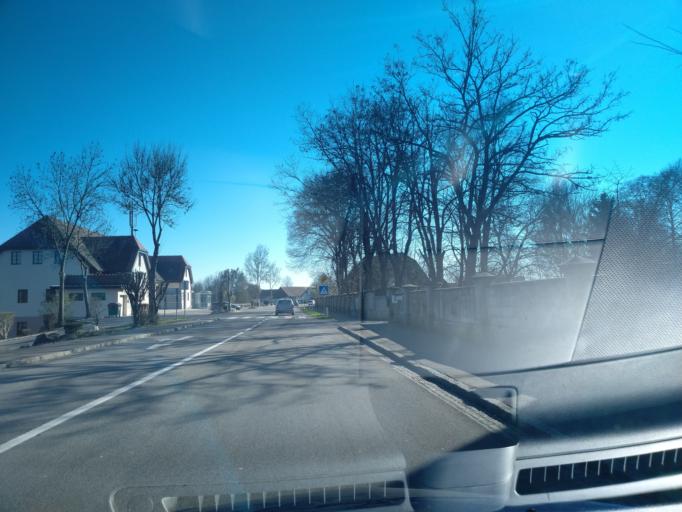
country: AT
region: Styria
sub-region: Politischer Bezirk Leibnitz
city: Stocking
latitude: 46.8540
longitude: 15.5378
